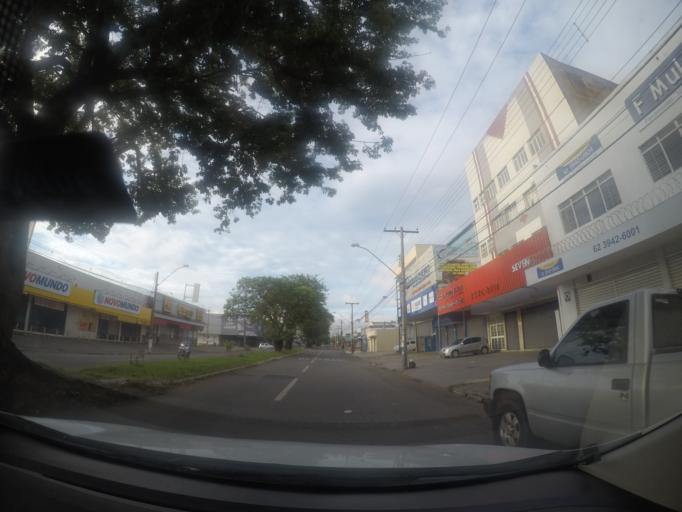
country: BR
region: Goias
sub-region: Goiania
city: Goiania
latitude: -16.6777
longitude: -49.3072
